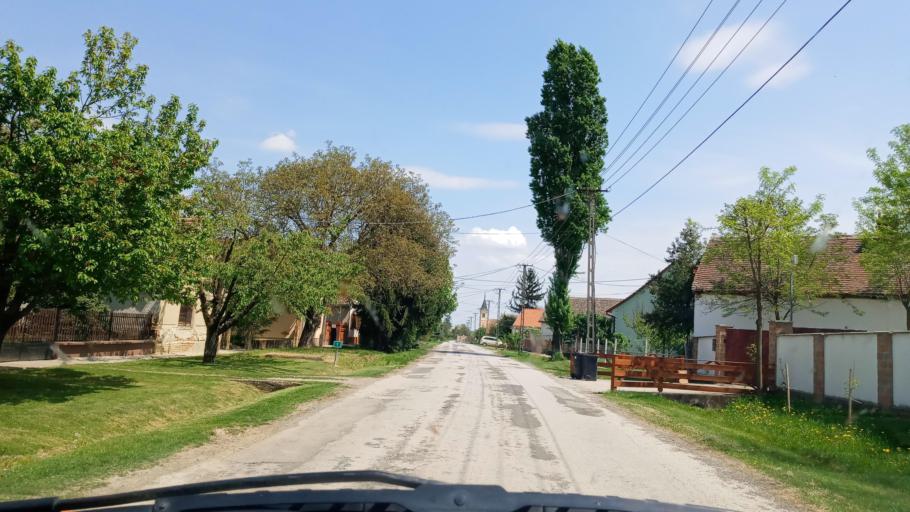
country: HU
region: Baranya
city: Villany
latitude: 45.8847
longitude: 18.4929
